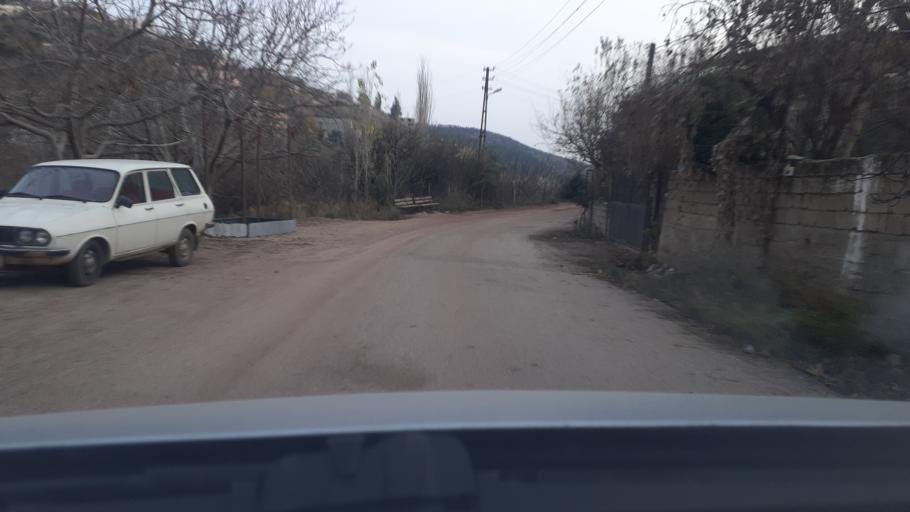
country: TR
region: Hatay
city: Kirikhan
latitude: 36.5360
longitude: 36.3140
